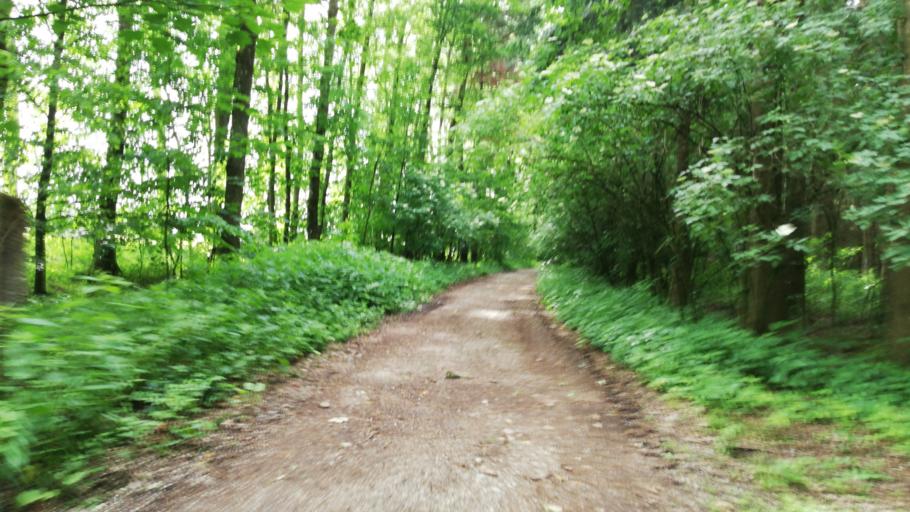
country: AT
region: Upper Austria
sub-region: Politischer Bezirk Grieskirchen
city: Bad Schallerbach
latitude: 48.2420
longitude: 13.9255
